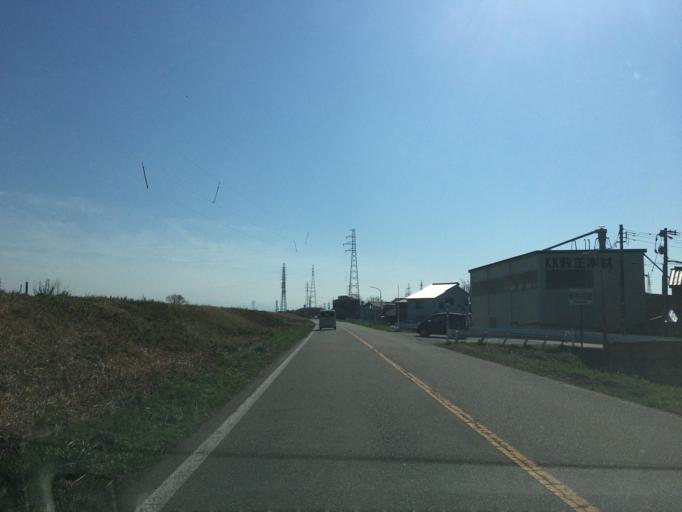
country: JP
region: Toyama
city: Nishishinminato
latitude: 36.7825
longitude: 137.0611
